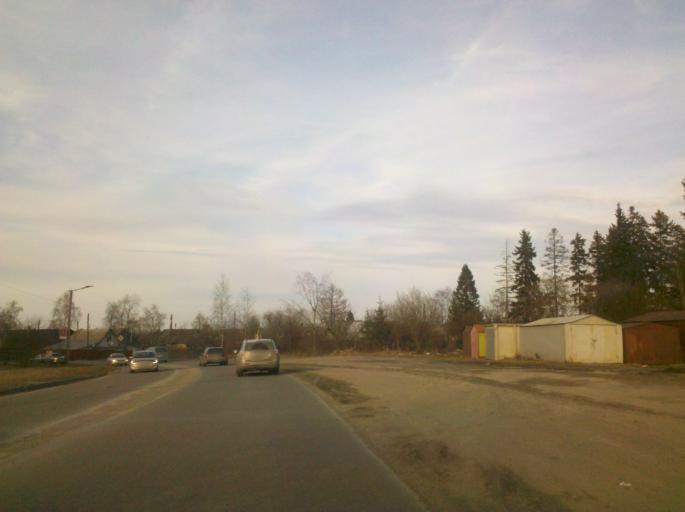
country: RU
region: Republic of Karelia
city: Petrozavodsk
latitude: 61.7614
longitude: 34.3862
